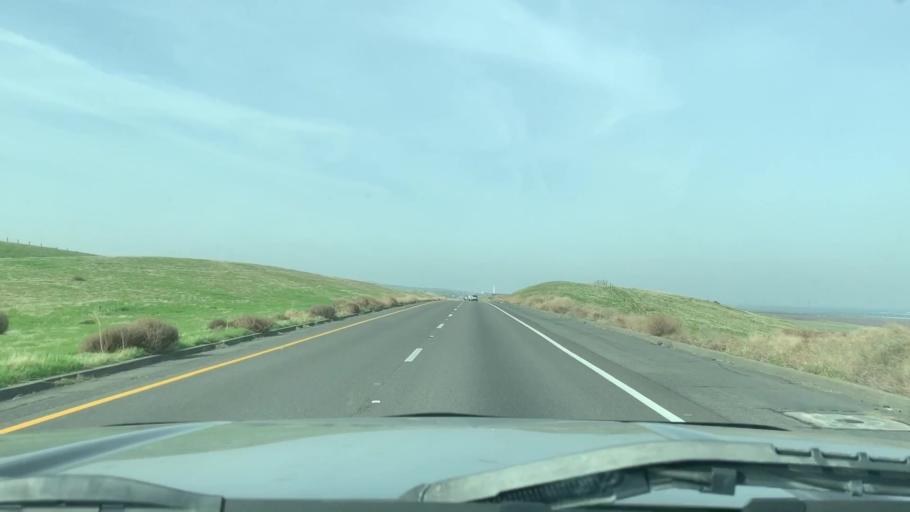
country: US
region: California
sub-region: Kings County
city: Kettleman City
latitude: 36.0297
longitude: -120.0208
